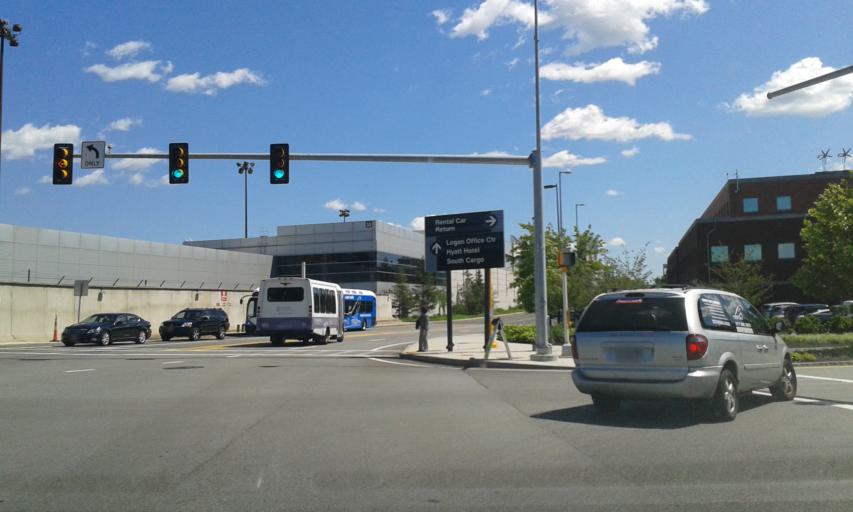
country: US
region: Massachusetts
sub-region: Suffolk County
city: Chelsea
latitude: 42.3652
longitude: -71.0253
